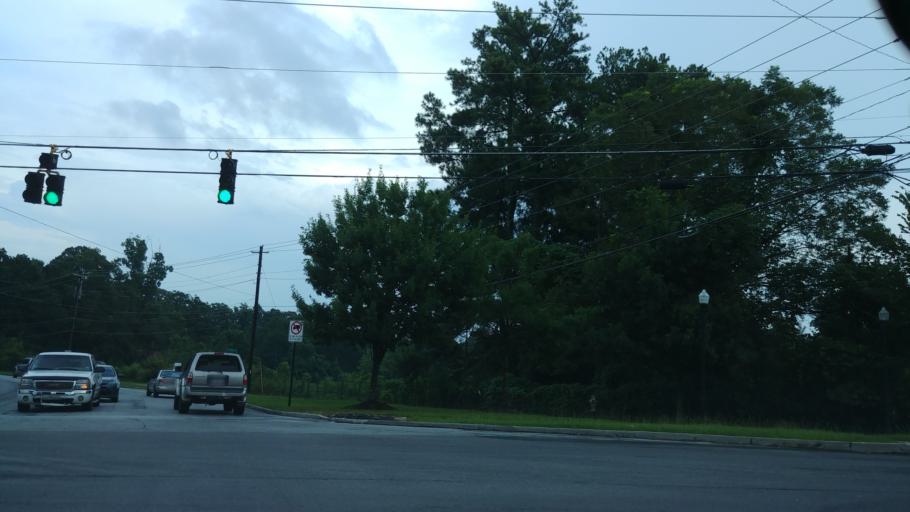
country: US
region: Georgia
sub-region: DeKalb County
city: Chamblee
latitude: 33.8921
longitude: -84.2990
